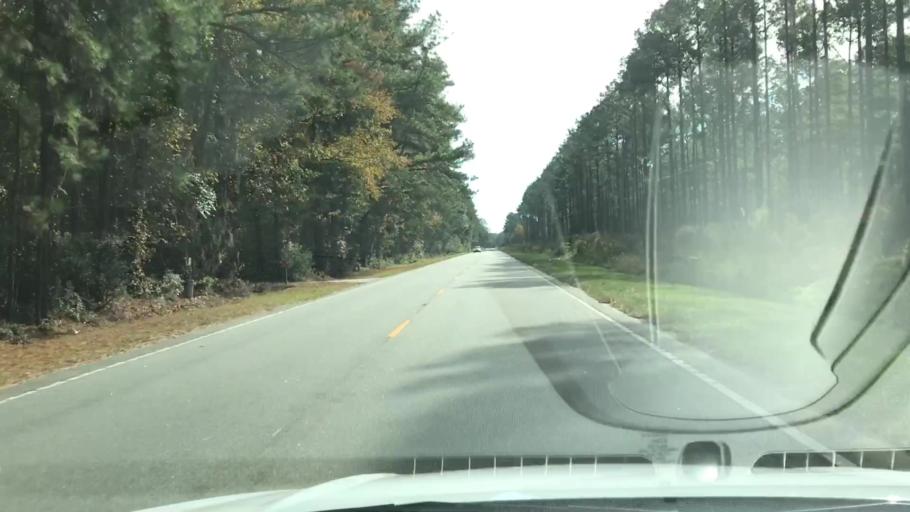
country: US
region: South Carolina
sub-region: Colleton County
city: Walterboro
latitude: 32.7880
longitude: -80.4773
